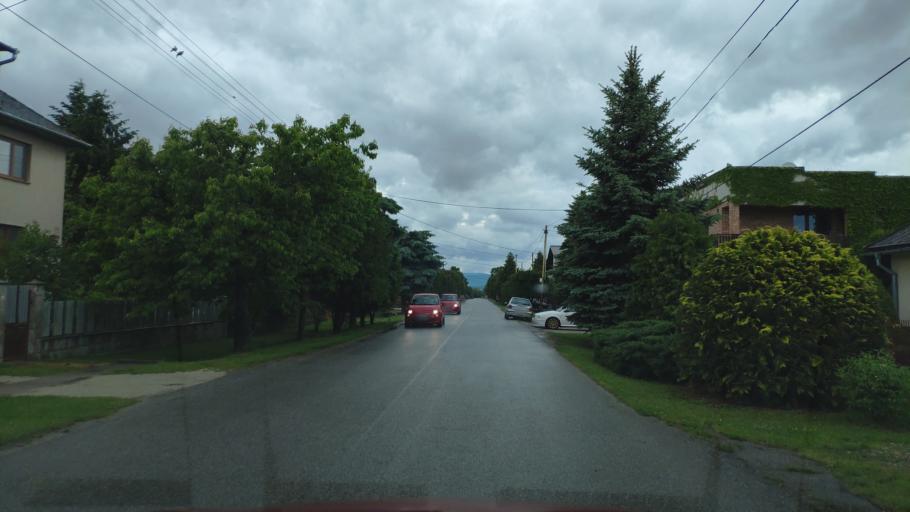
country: SK
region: Kosicky
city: Moldava nad Bodvou
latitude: 48.5337
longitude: 21.1098
